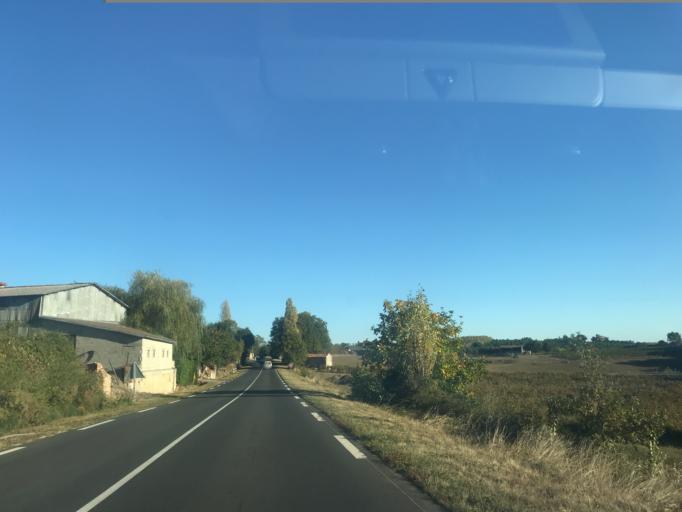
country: FR
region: Poitou-Charentes
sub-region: Departement de la Charente-Maritime
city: Montguyon
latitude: 45.1838
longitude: -0.1290
